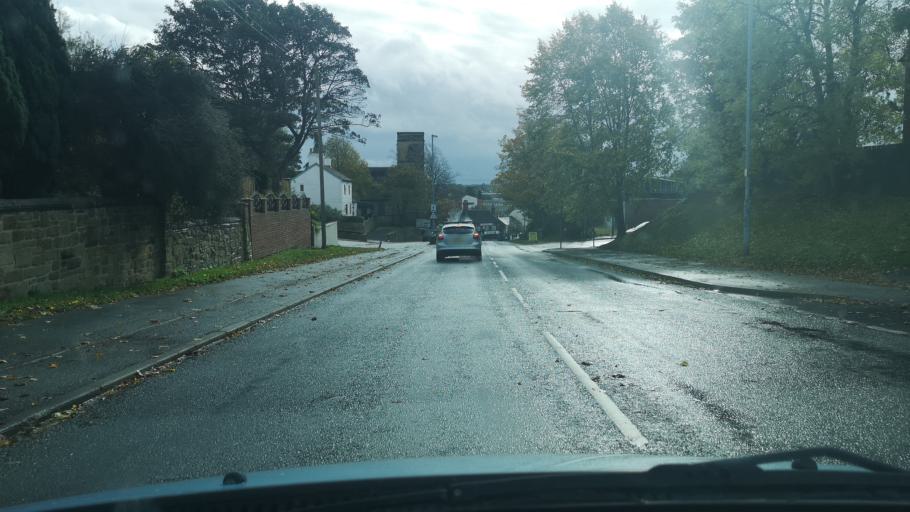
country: GB
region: England
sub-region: City and Borough of Wakefield
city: Hemsworth
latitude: 53.6154
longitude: -1.3539
